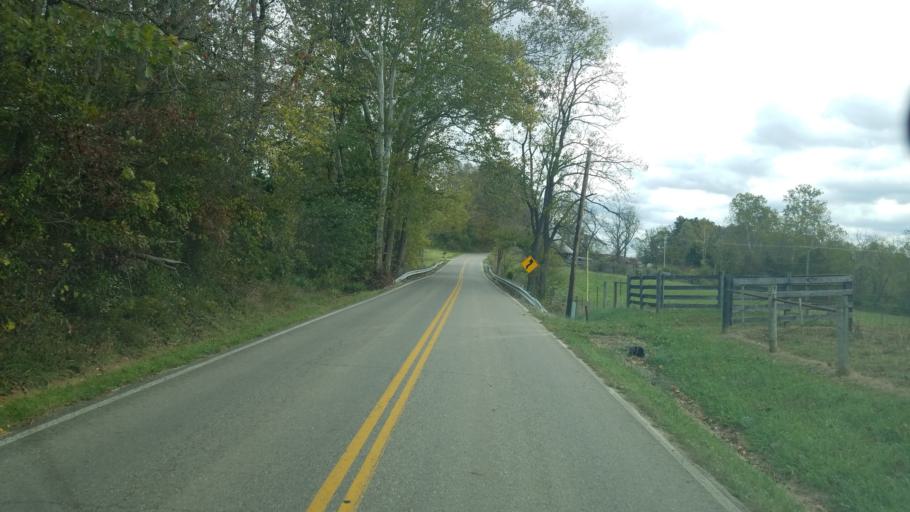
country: US
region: Ohio
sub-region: Jackson County
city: Jackson
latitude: 39.1437
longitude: -82.6578
